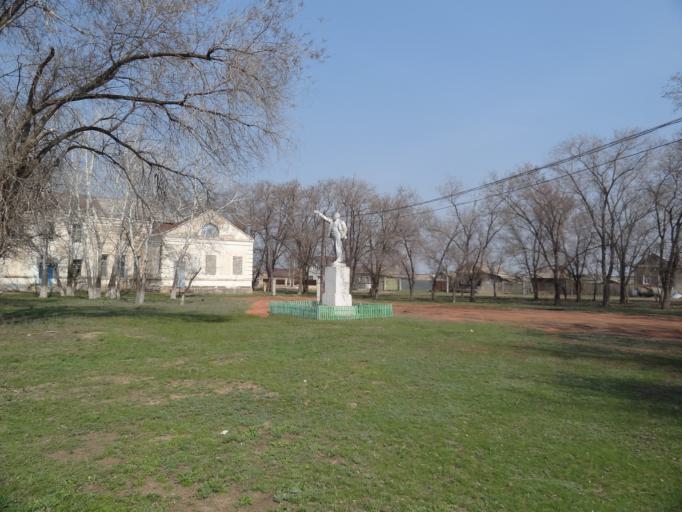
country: RU
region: Saratov
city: Privolzhskiy
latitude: 51.3042
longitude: 45.9596
